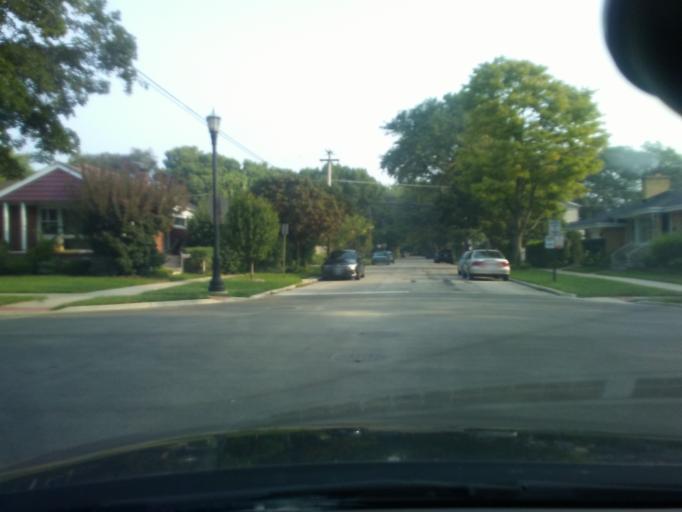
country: US
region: Illinois
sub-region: Cook County
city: Evanston
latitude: 42.0201
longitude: -87.7019
